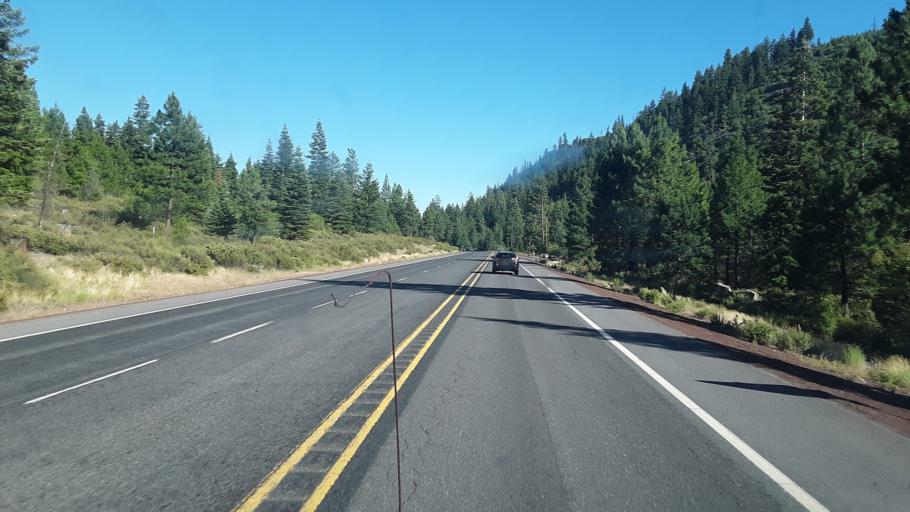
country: US
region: Oregon
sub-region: Klamath County
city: Klamath Falls
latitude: 42.3308
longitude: -121.9574
